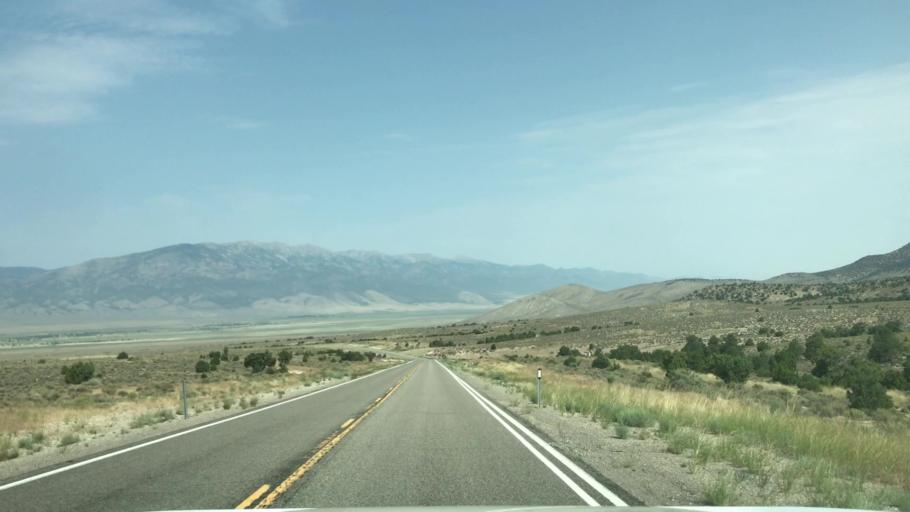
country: US
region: Nevada
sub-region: White Pine County
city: McGill
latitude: 39.1682
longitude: -114.3665
